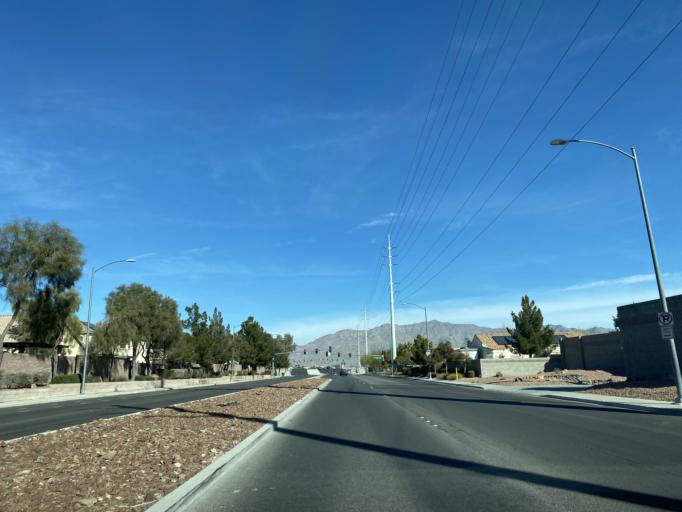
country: US
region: Nevada
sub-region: Clark County
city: North Las Vegas
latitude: 36.2707
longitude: -115.2251
